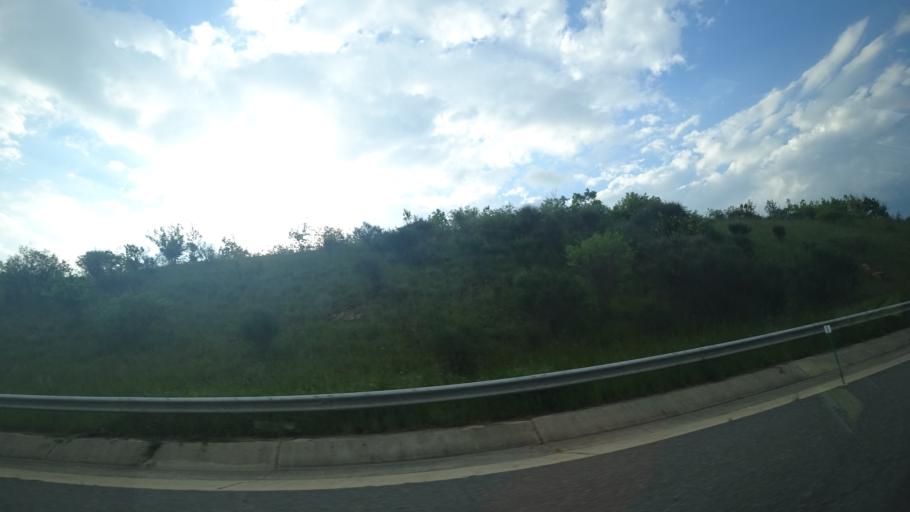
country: FR
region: Midi-Pyrenees
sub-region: Departement de l'Aveyron
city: Creissels
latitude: 44.1558
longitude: 3.0209
